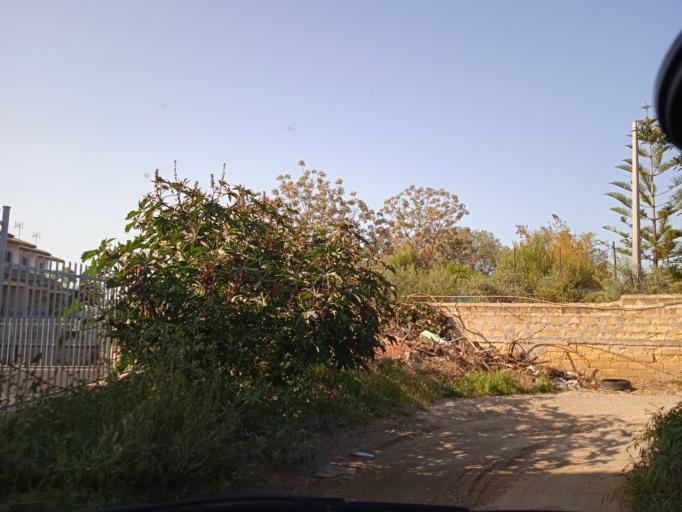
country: IT
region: Sicily
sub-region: Palermo
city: Villabate
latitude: 38.0817
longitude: 13.4515
